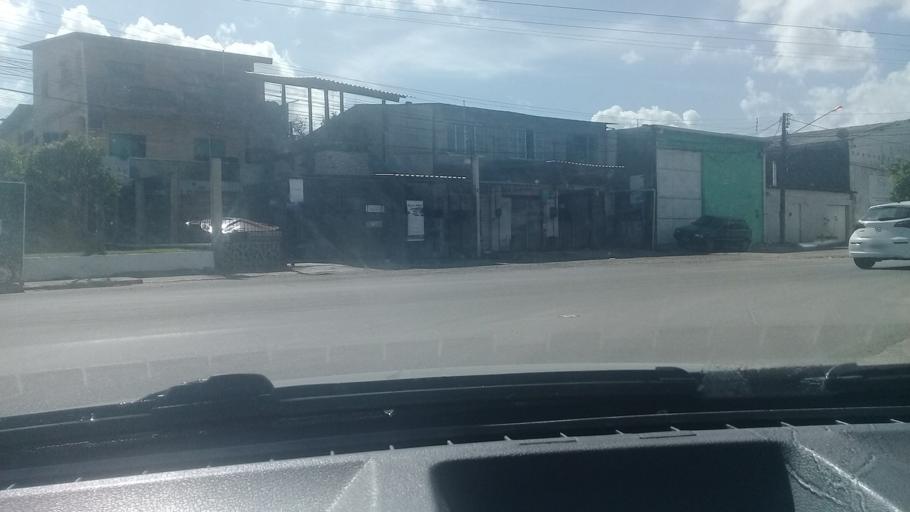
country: BR
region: Pernambuco
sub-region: Jaboatao Dos Guararapes
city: Jaboatao dos Guararapes
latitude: -8.0926
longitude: -35.0233
